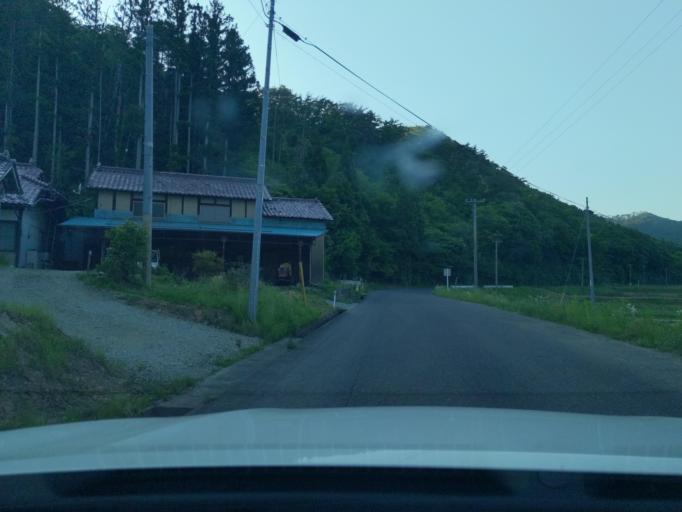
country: JP
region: Fukushima
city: Motomiya
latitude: 37.5027
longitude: 140.3257
